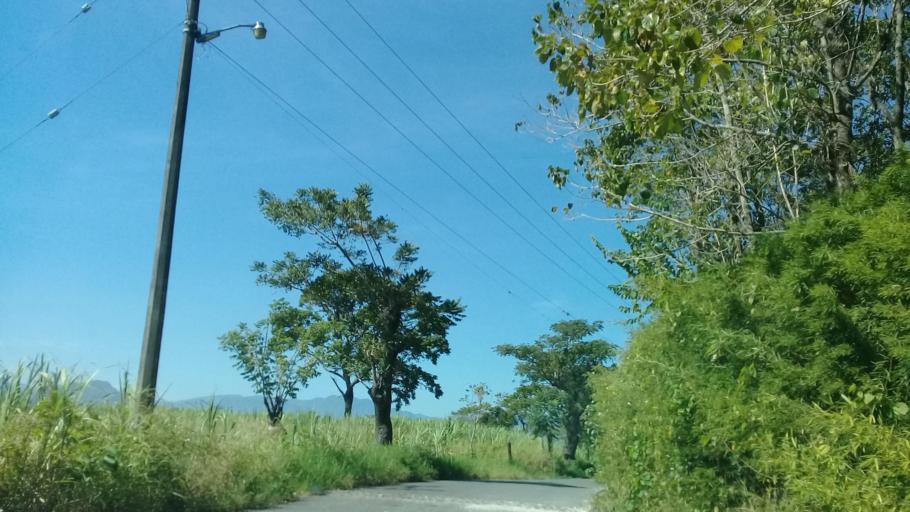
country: MX
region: Veracruz
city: Amatlan de los Reyes
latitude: 18.8551
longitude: -96.9078
